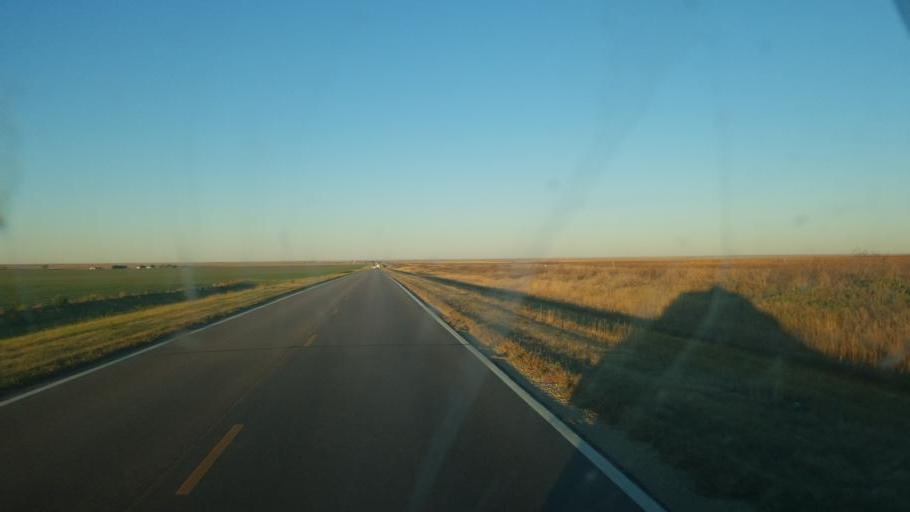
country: US
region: Kansas
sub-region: Wallace County
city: Sharon Springs
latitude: 38.8654
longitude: -101.9902
